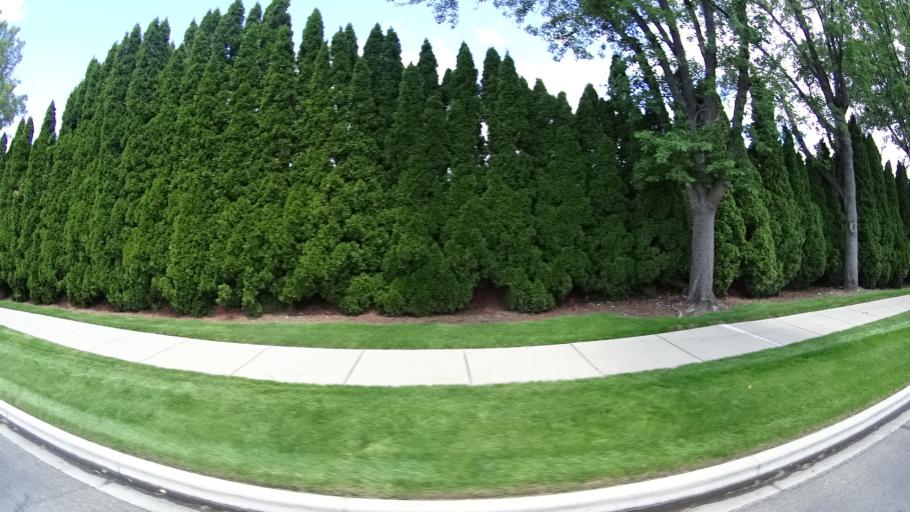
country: US
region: Idaho
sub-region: Ada County
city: Eagle
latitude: 43.6588
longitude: -116.3522
